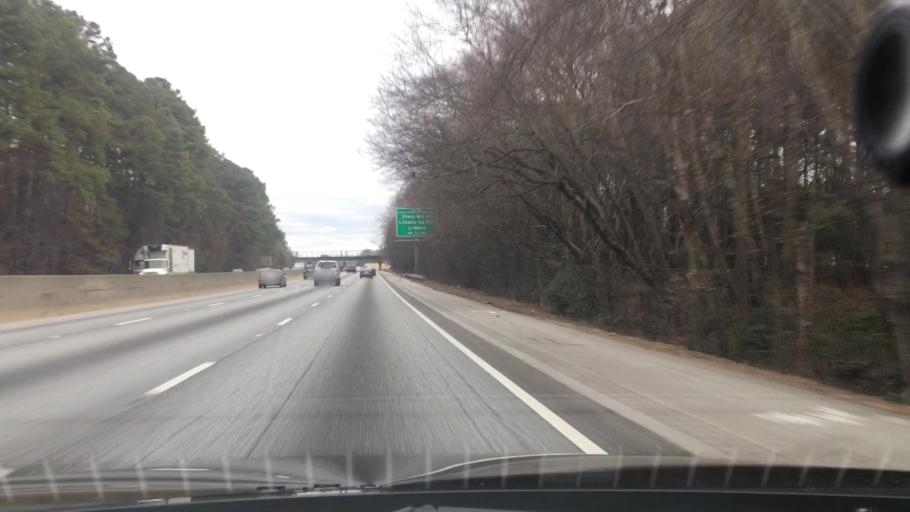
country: US
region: Georgia
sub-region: DeKalb County
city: Pine Mountain
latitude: 33.7031
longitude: -84.1511
